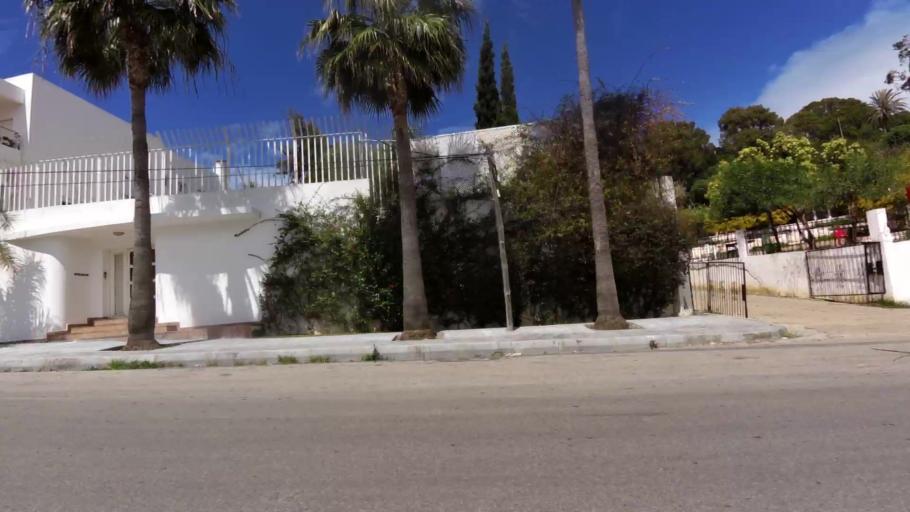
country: MA
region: Tanger-Tetouan
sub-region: Tanger-Assilah
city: Tangier
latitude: 35.7794
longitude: -5.8592
